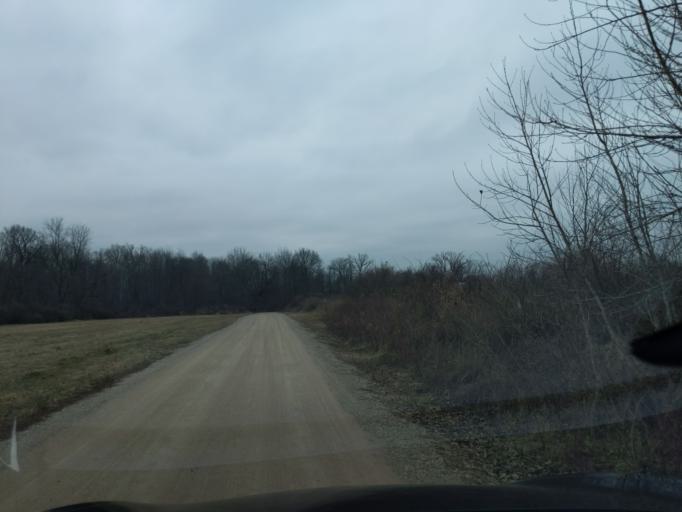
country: US
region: Michigan
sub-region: Eaton County
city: Potterville
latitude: 42.6204
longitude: -84.7572
